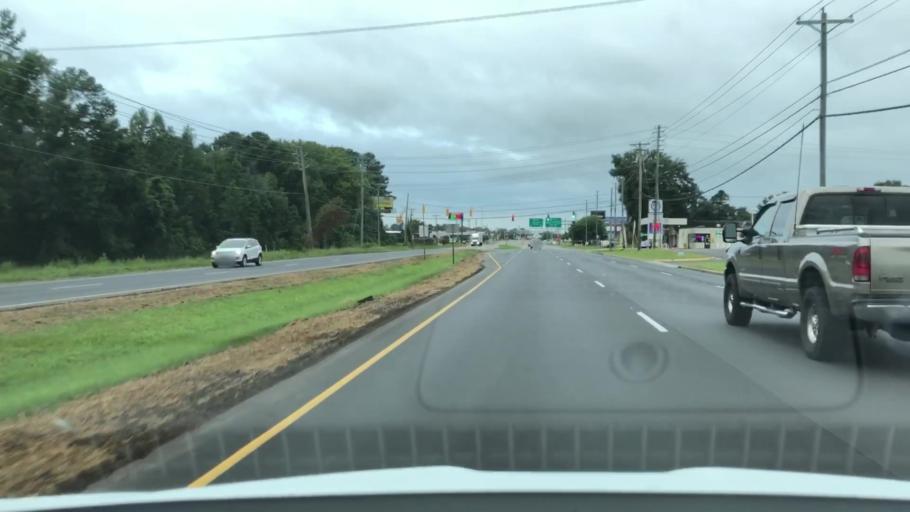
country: US
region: North Carolina
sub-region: Lenoir County
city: Kinston
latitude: 35.2652
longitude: -77.6368
